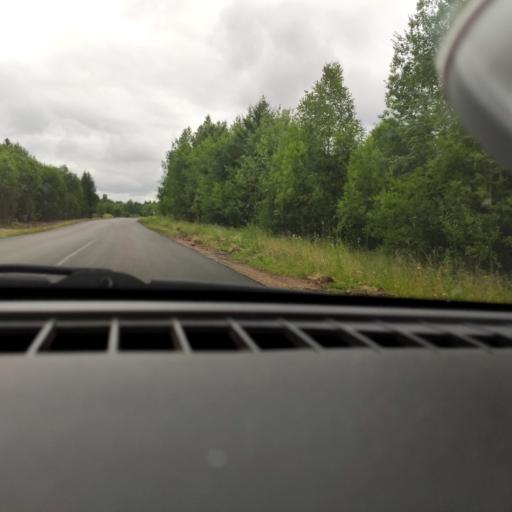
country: RU
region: Perm
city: Polazna
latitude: 58.3349
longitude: 56.1948
